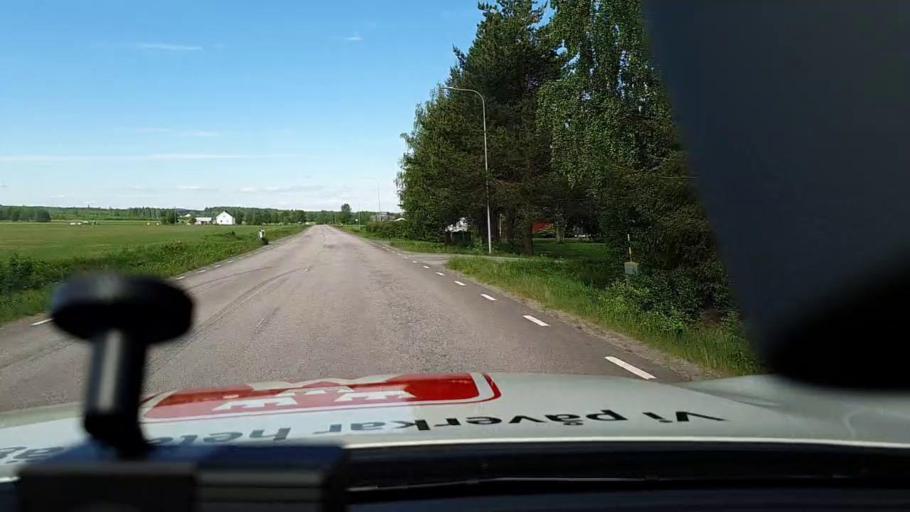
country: SE
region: Norrbotten
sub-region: Lulea Kommun
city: Sodra Sunderbyn
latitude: 65.6488
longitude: 21.8763
